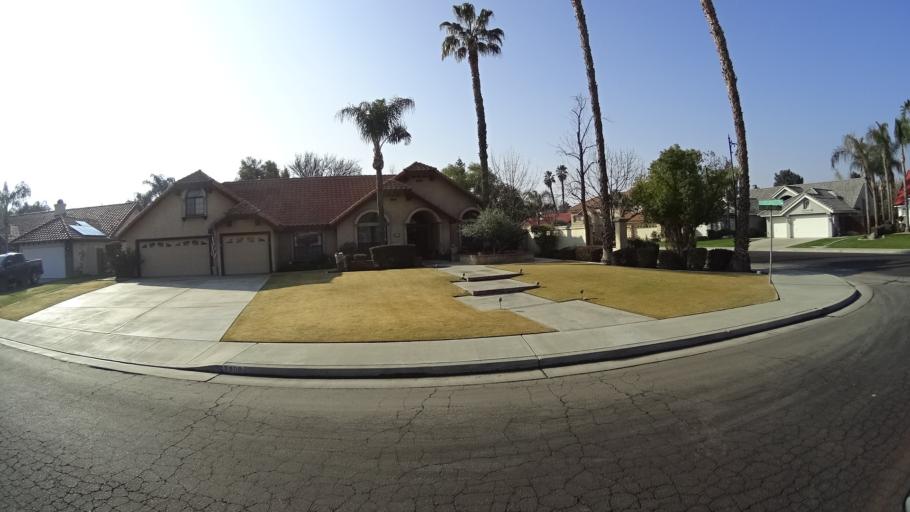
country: US
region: California
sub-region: Kern County
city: Greenacres
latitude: 35.3361
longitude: -119.0847
